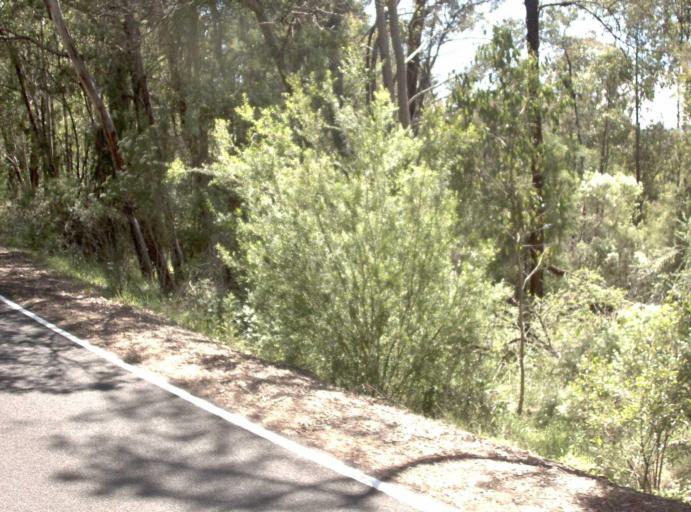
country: AU
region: Victoria
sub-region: East Gippsland
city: Lakes Entrance
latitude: -37.3529
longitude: 148.2280
